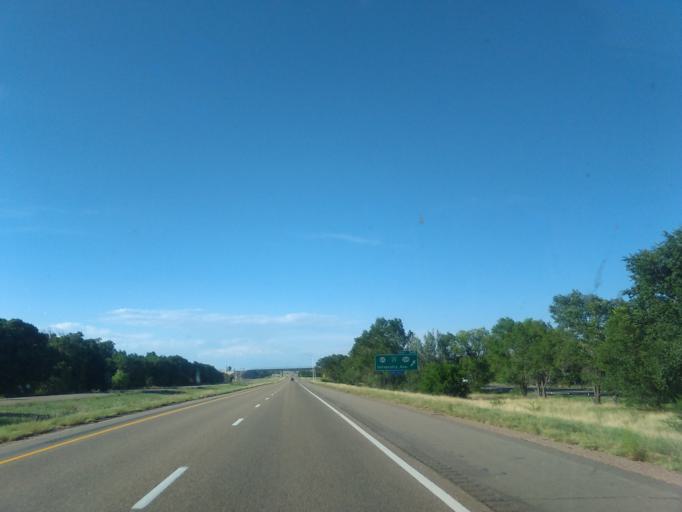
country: US
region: New Mexico
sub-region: San Miguel County
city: Las Vegas
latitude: 35.5871
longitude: -105.2113
